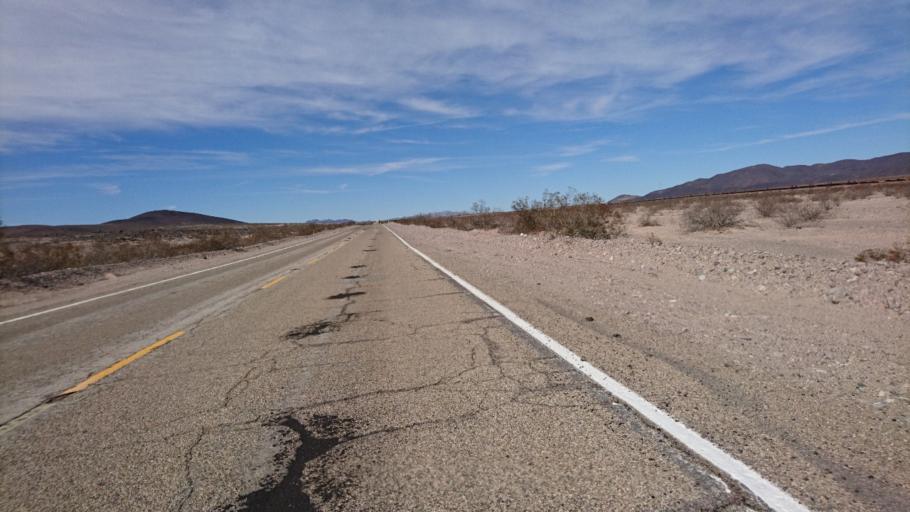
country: US
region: California
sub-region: San Bernardino County
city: Twentynine Palms
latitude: 34.6895
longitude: -116.0420
